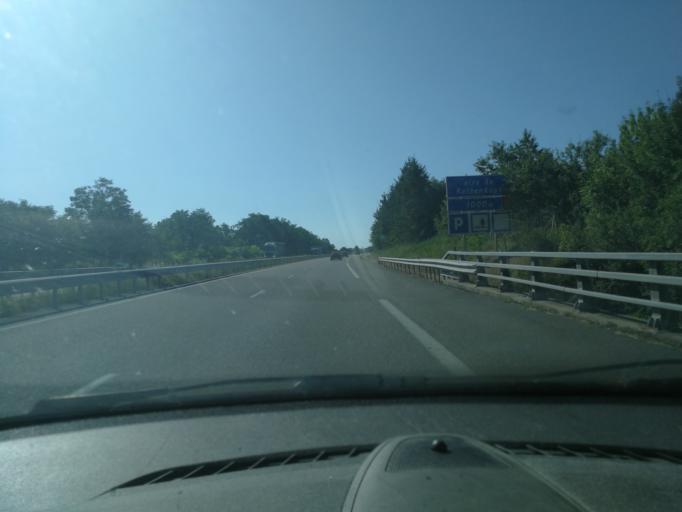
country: FR
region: Alsace
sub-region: Departement du Bas-Rhin
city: Drulingen
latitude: 48.8347
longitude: 7.1412
